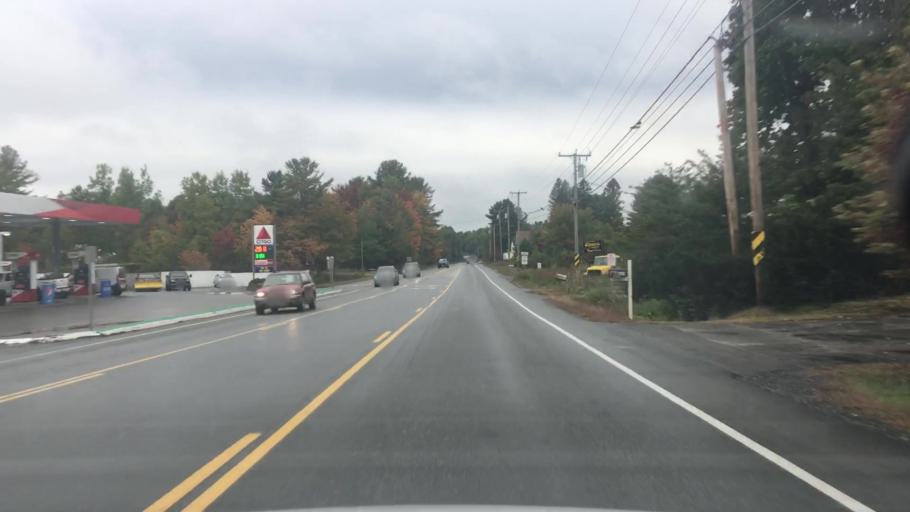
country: US
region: Maine
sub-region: Kennebec County
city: Augusta
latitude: 44.3746
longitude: -69.7962
